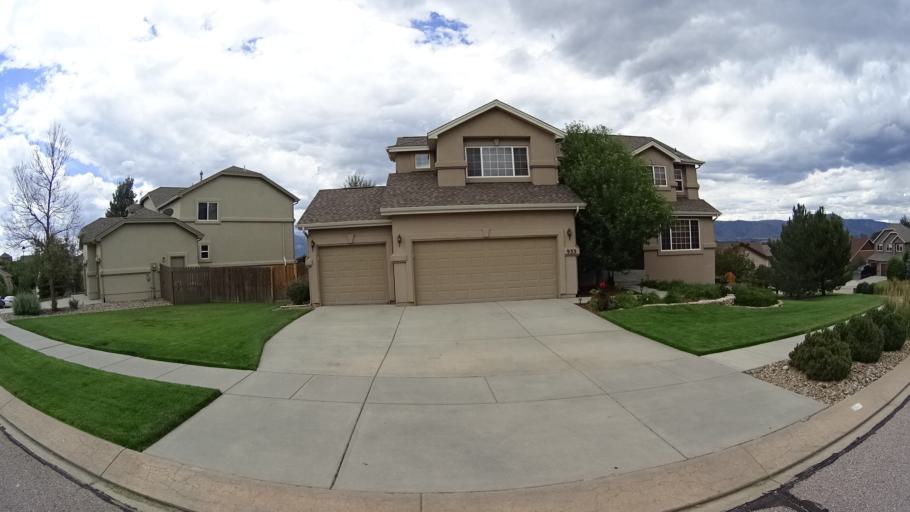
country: US
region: Colorado
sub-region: El Paso County
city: Gleneagle
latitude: 39.0338
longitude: -104.8106
